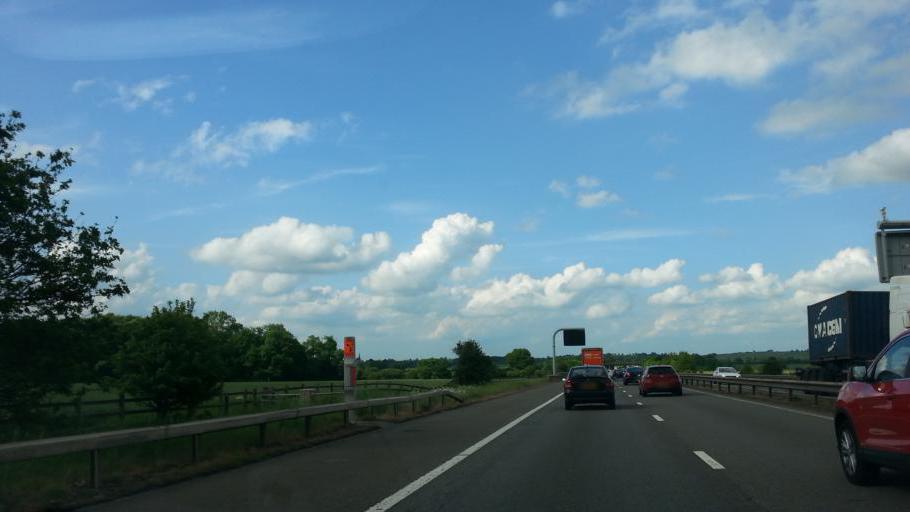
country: GB
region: England
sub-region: Derbyshire
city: Netherseal
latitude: 52.6455
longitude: -1.5959
